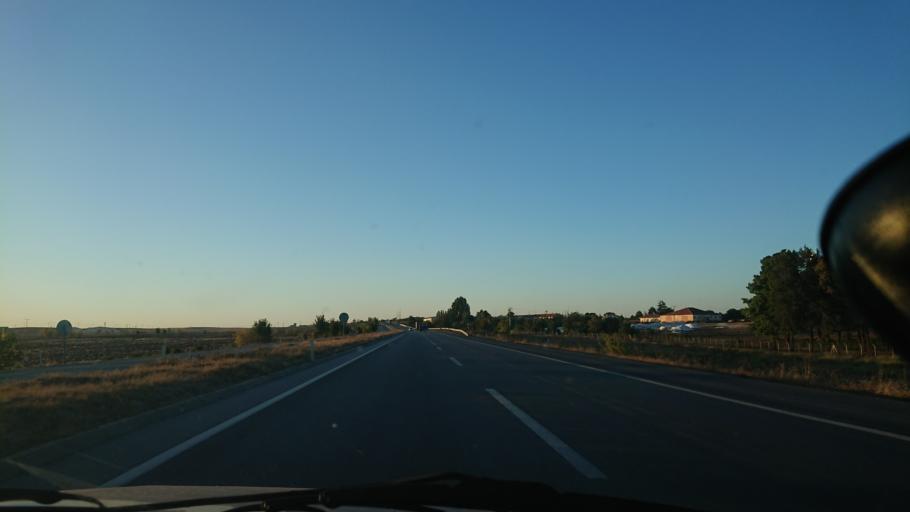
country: TR
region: Eskisehir
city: Mahmudiye
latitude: 39.4783
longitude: 30.9902
